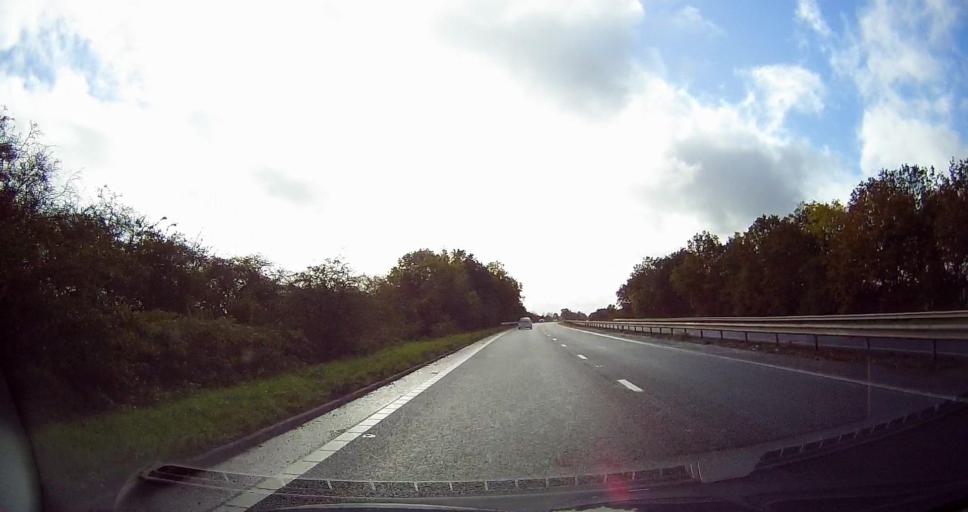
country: GB
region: England
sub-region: Warwickshire
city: Curdworth
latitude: 52.5613
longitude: -1.7701
